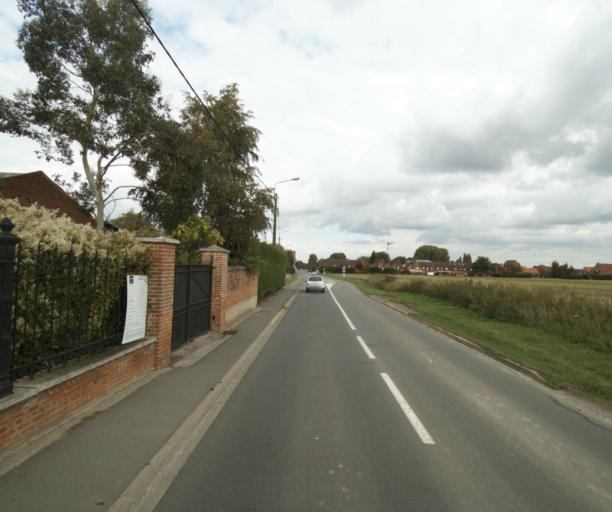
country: FR
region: Nord-Pas-de-Calais
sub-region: Departement du Nord
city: Perenchies
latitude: 50.6622
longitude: 2.9626
